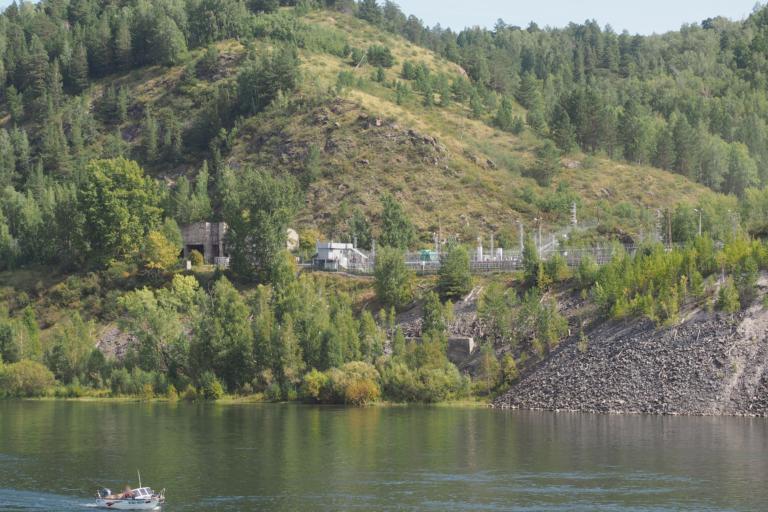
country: RU
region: Krasnoyarskiy
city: Zheleznogorsk
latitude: 56.3458
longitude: 93.5795
